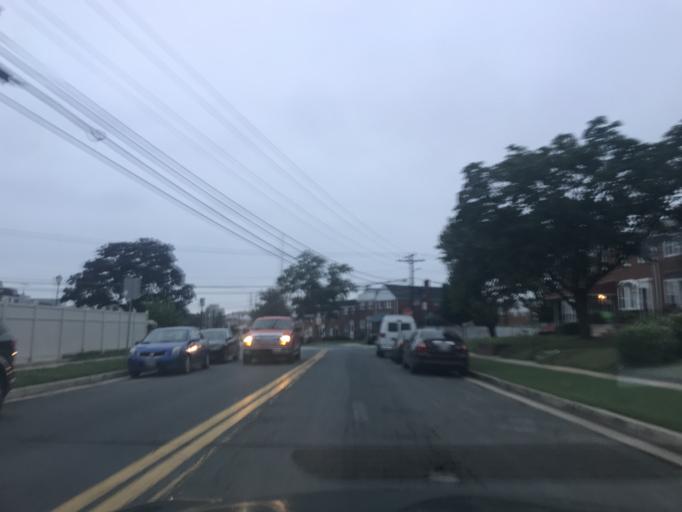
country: US
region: Maryland
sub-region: Baltimore County
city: Dundalk
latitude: 39.2640
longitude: -76.4959
